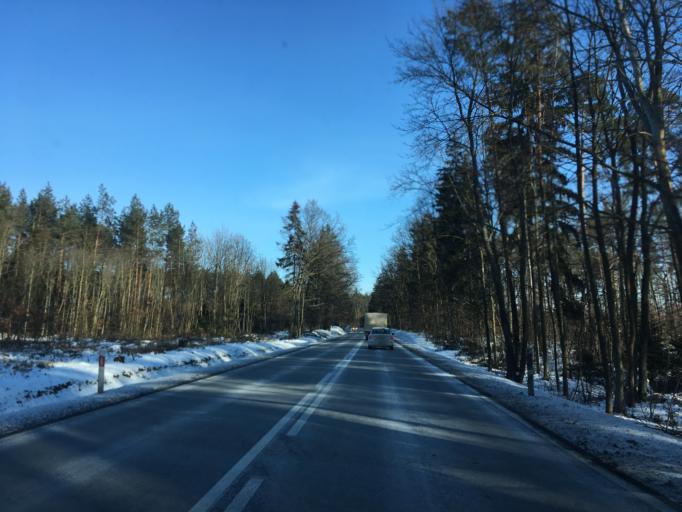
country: PL
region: Pomeranian Voivodeship
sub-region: Powiat koscierski
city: Koscierzyna
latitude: 54.1114
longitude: 17.9221
